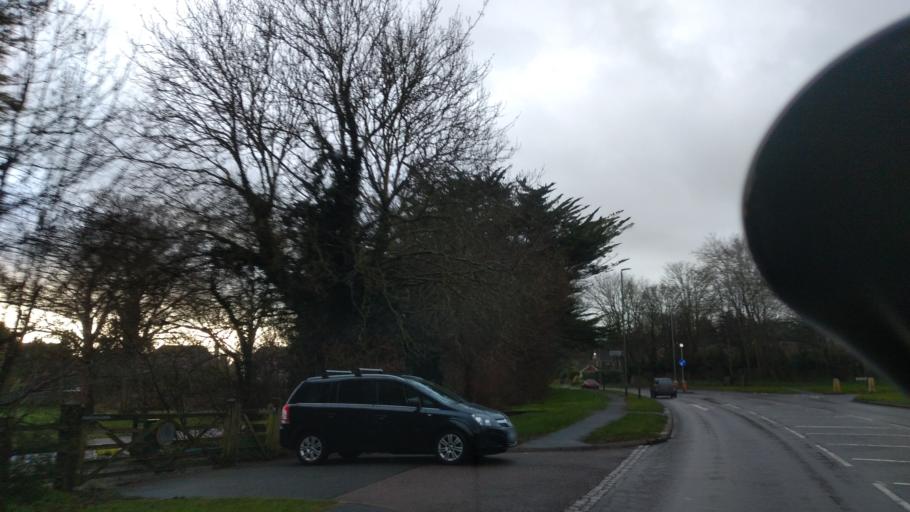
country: GB
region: England
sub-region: East Sussex
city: Eastbourne
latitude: 50.7933
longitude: 0.2564
